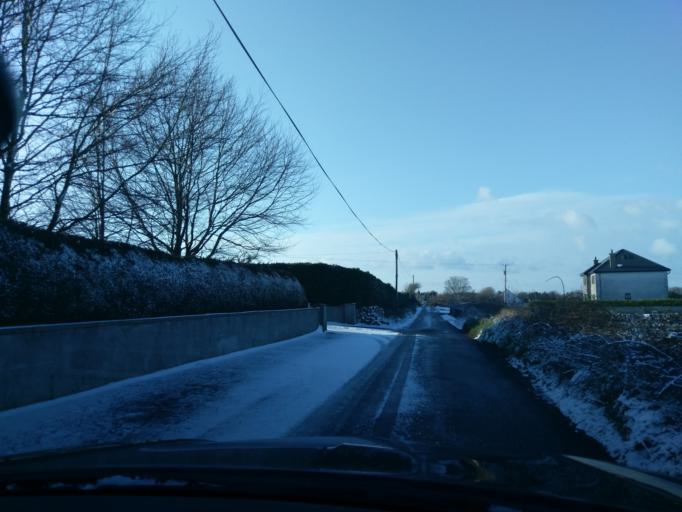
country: IE
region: Connaught
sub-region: County Galway
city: Athenry
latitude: 53.1865
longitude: -8.7239
